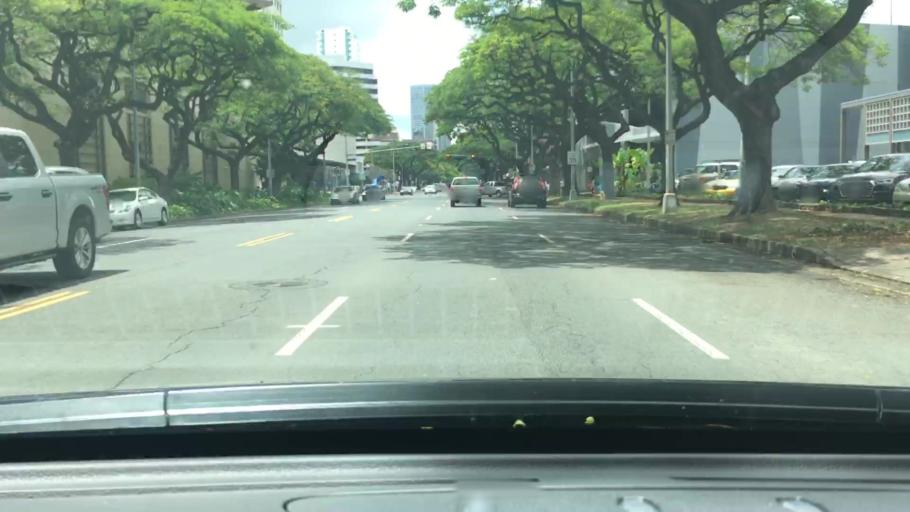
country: US
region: Hawaii
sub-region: Honolulu County
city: Honolulu
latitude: 21.2926
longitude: -157.8413
